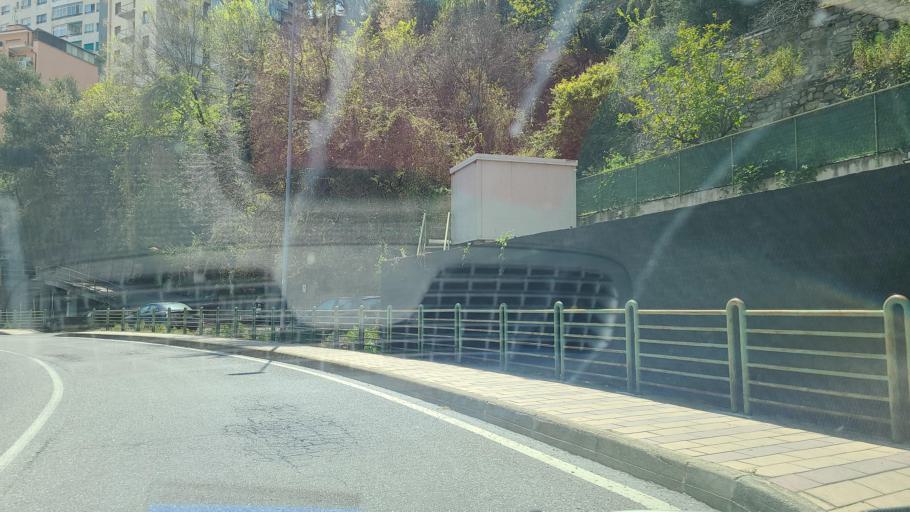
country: IT
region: Liguria
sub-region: Provincia di Imperia
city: San Remo
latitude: 43.8222
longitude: 7.7666
